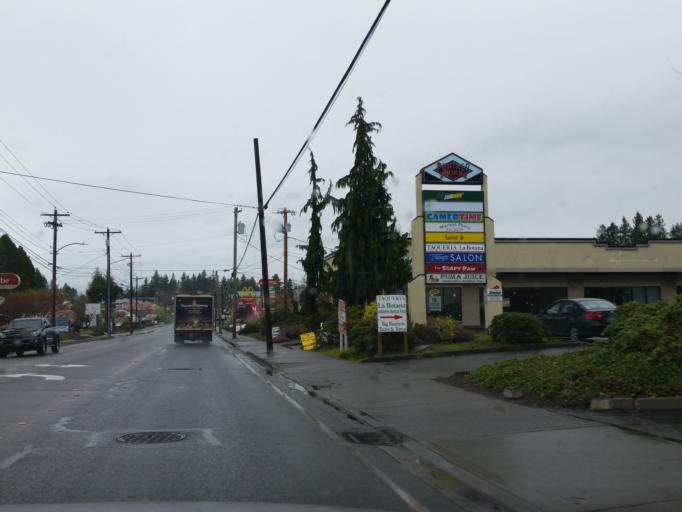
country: US
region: Washington
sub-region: Snohomish County
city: Snohomish
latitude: 47.9212
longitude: -122.0980
